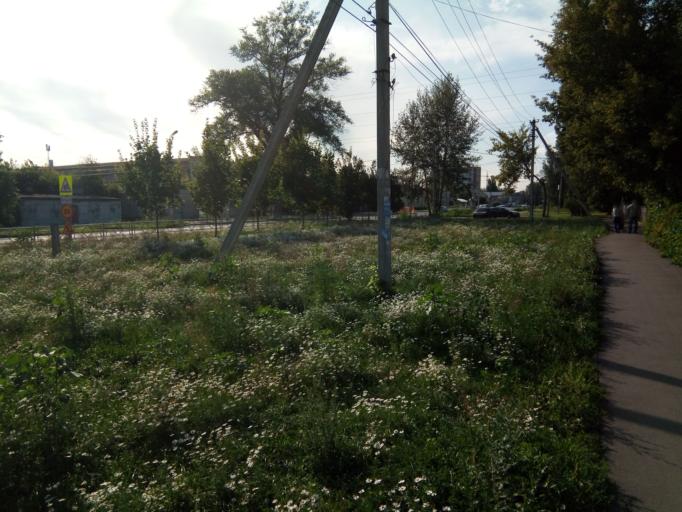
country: RU
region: Lipetsk
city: Lipetsk
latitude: 52.6287
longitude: 39.5558
